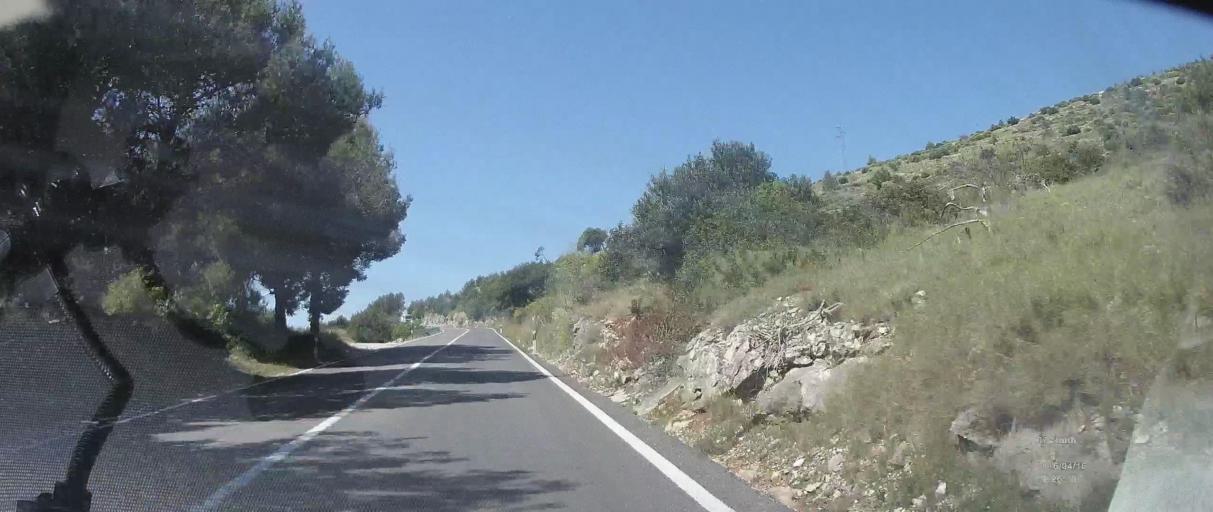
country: HR
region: Splitsko-Dalmatinska
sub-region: Grad Trogir
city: Trogir
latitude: 43.5173
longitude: 16.2121
